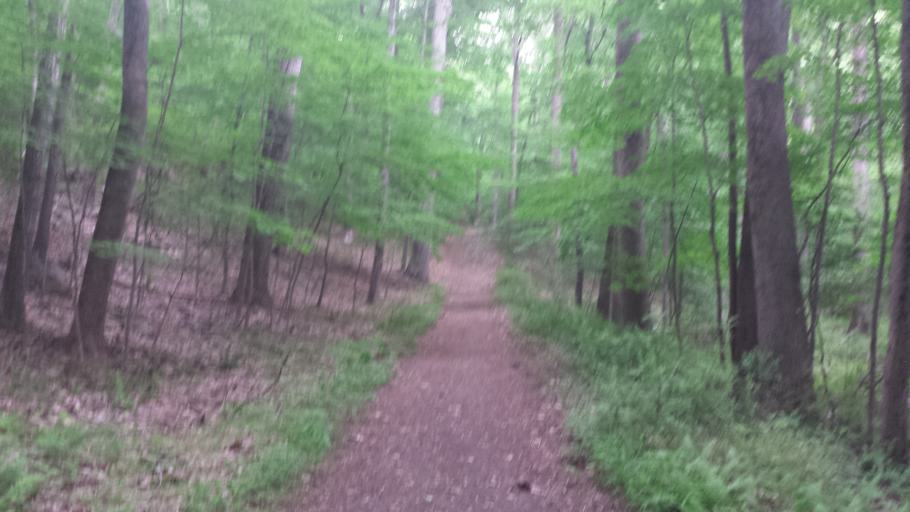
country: US
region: New York
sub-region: Westchester County
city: Pound Ridge
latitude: 41.2683
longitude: -73.5948
